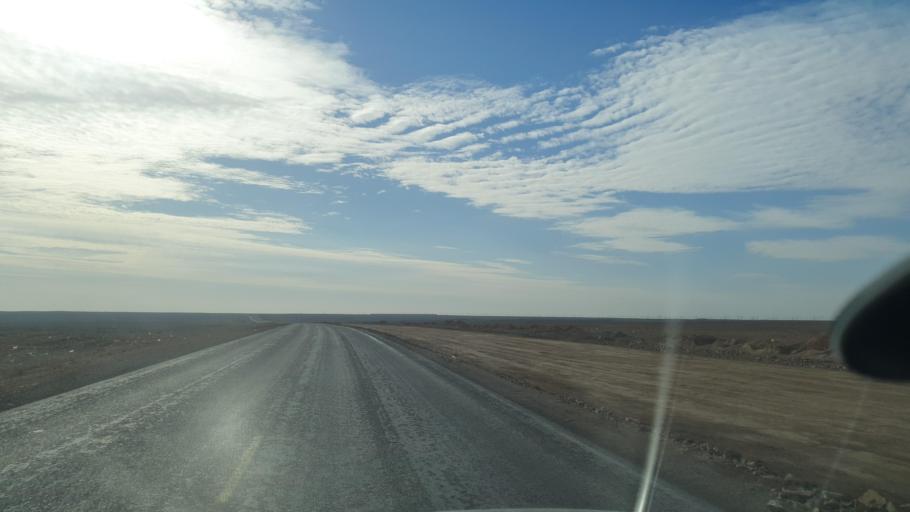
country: KZ
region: Qaraghandy
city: Saryshaghan
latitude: 45.9695
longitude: 73.5482
